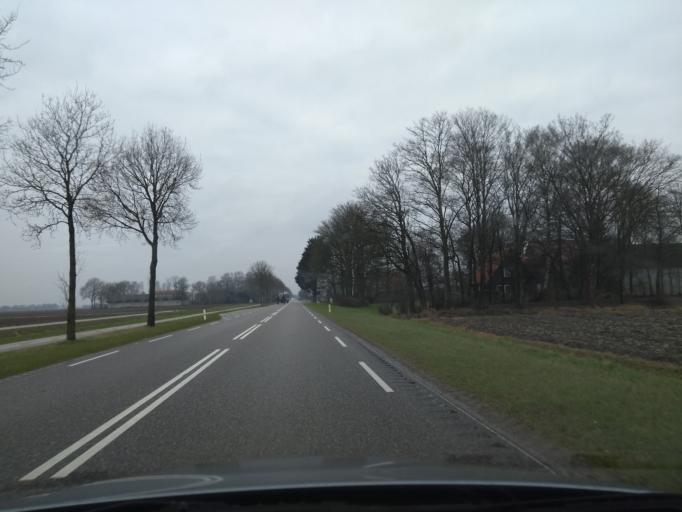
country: NL
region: Overijssel
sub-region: Gemeente Steenwijkerland
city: Vollenhove
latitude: 52.6943
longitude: 5.9194
